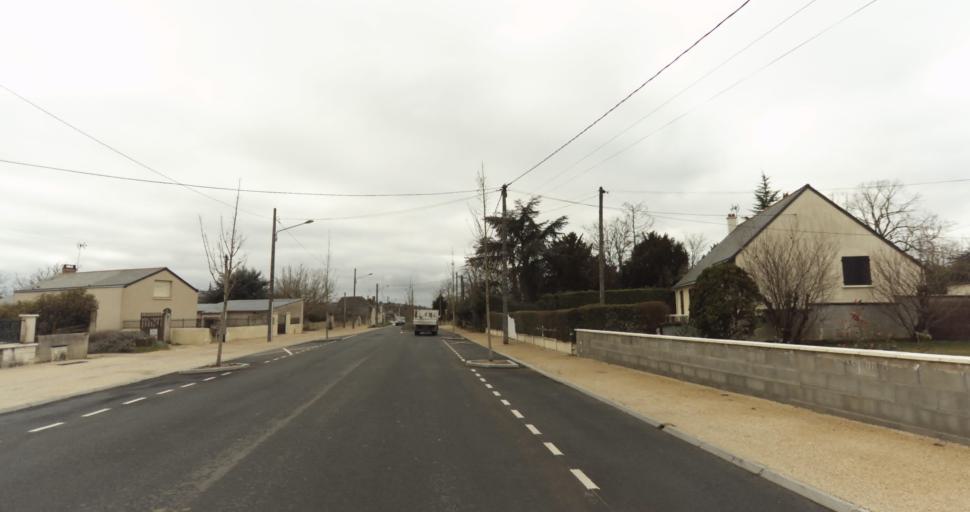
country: FR
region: Pays de la Loire
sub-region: Departement de Maine-et-Loire
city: Montreuil-Bellay
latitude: 47.1404
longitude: -0.1544
